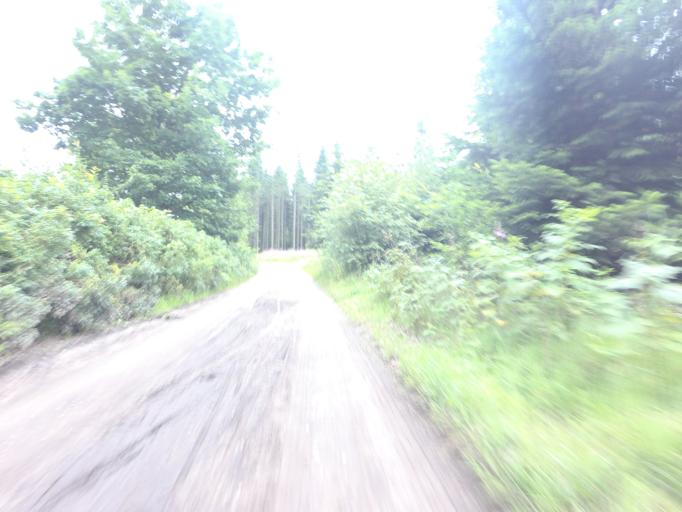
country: DK
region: Central Jutland
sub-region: Silkeborg Kommune
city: Virklund
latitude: 56.0241
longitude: 9.4960
